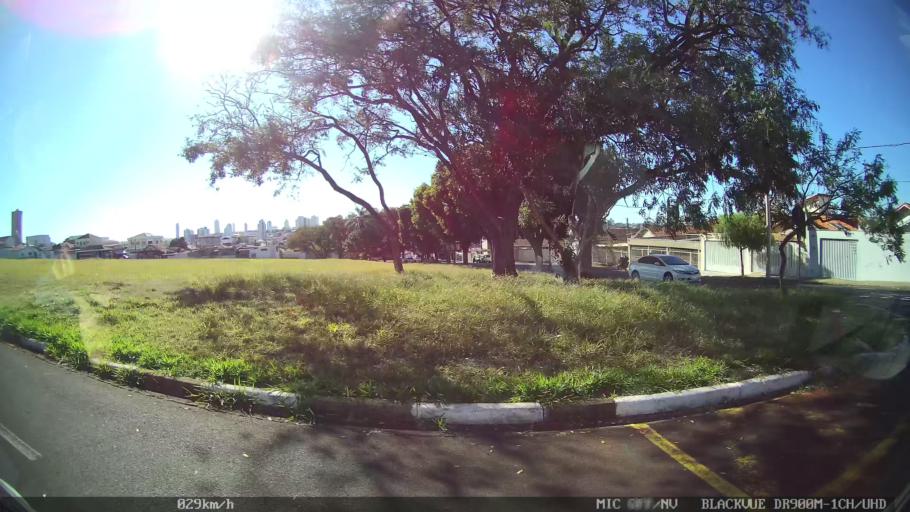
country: BR
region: Sao Paulo
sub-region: Franca
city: Franca
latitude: -20.5440
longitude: -47.4128
